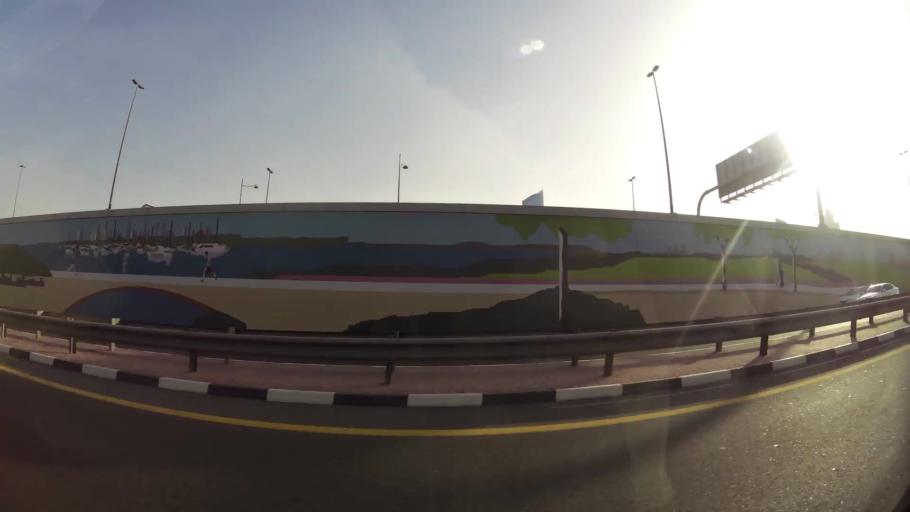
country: AE
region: Ash Shariqah
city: Sharjah
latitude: 25.2309
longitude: 55.3526
